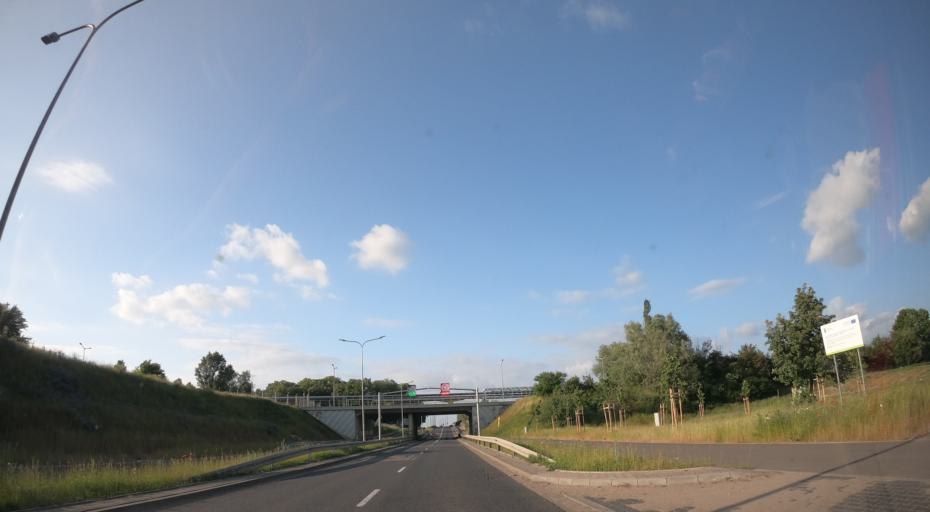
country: PL
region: Lubusz
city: Gorzow Wielkopolski
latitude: 52.7496
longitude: 15.2771
